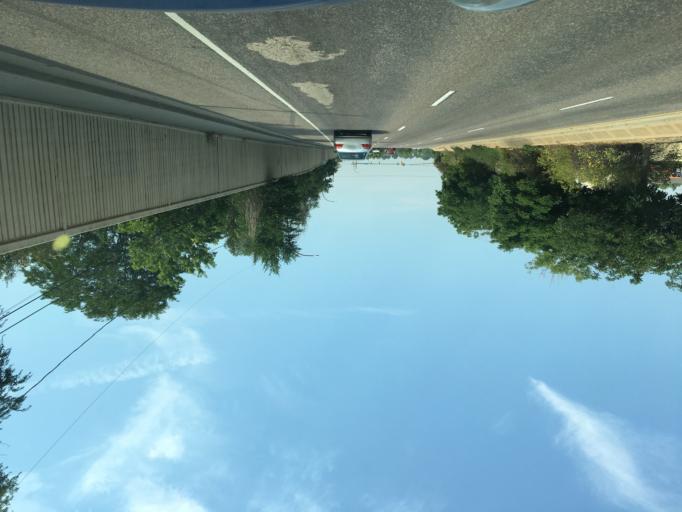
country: US
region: Colorado
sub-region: Jefferson County
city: Arvada
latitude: 39.8108
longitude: -105.0795
